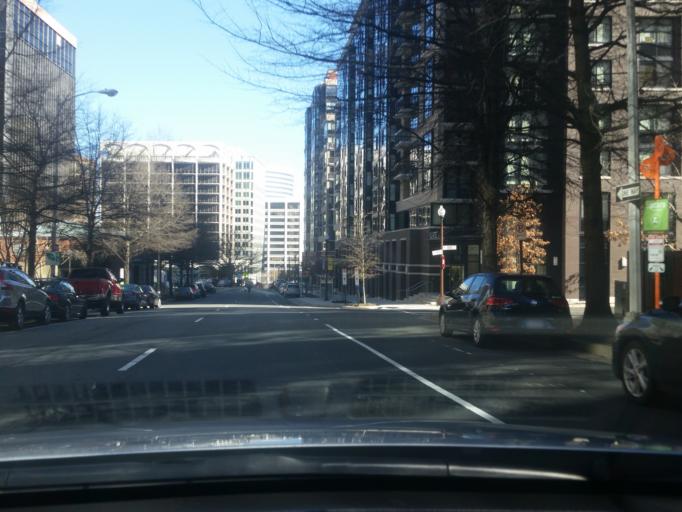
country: US
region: Virginia
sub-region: Arlington County
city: Arlington
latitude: 38.8936
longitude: -77.0760
